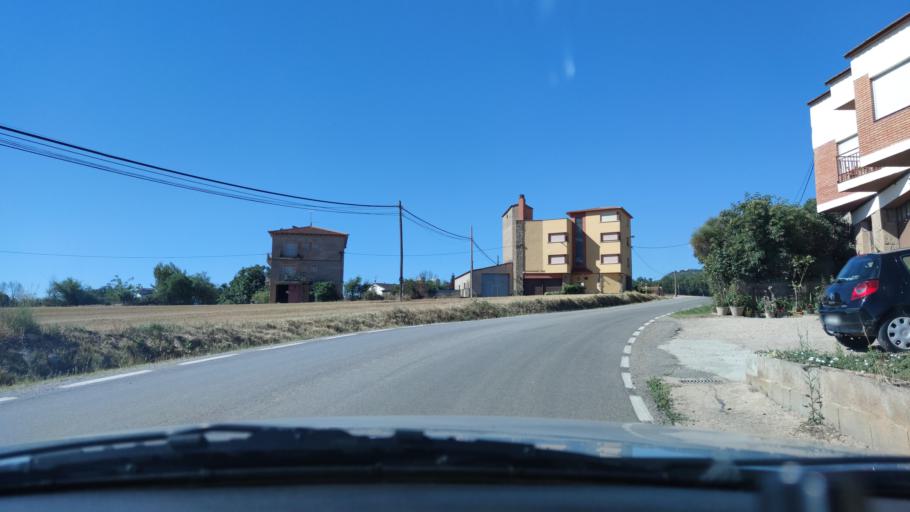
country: ES
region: Catalonia
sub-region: Provincia de Lleida
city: Solsona
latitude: 41.9846
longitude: 1.5060
